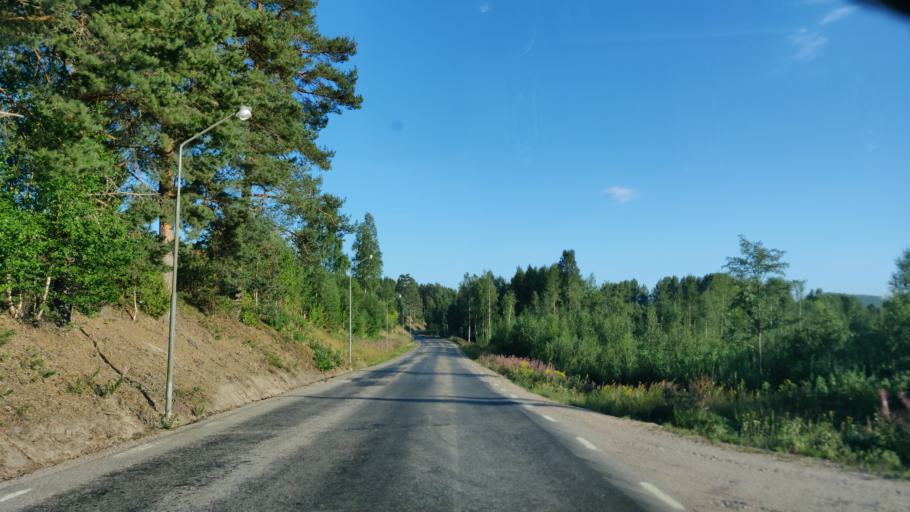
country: SE
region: Vaermland
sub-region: Hagfors Kommun
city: Ekshaerad
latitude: 60.1831
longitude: 13.5243
